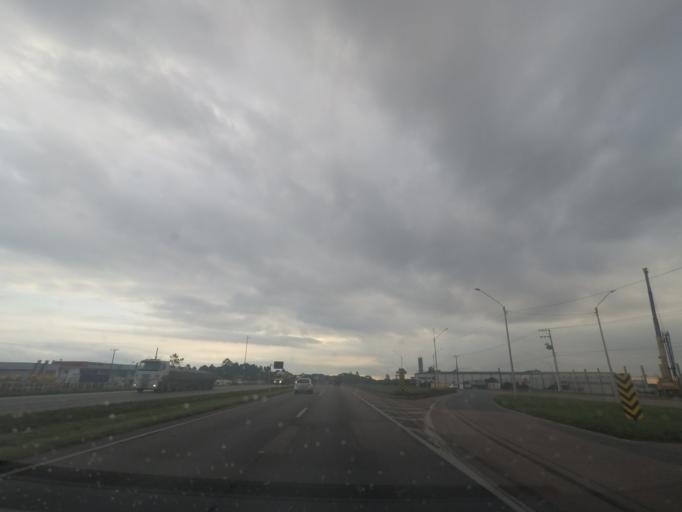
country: BR
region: Parana
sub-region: Sao Jose Dos Pinhais
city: Sao Jose dos Pinhais
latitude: -25.5715
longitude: -49.1960
